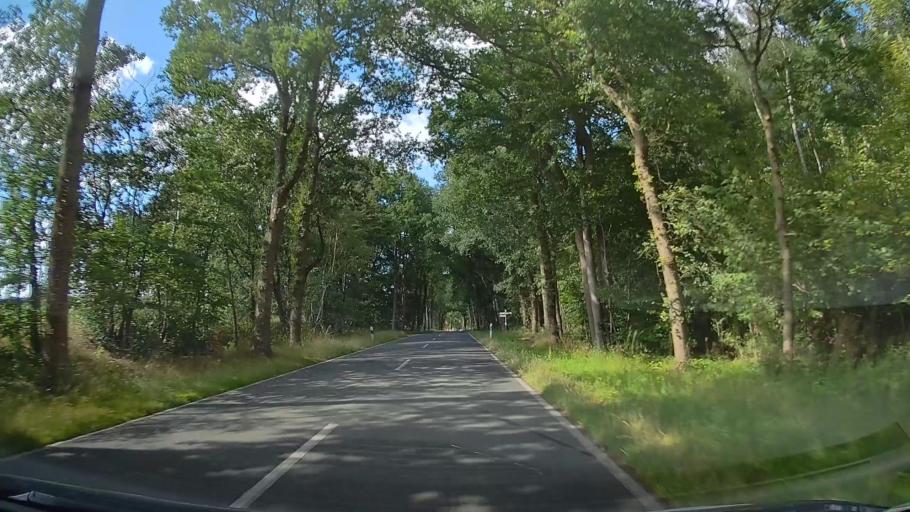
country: DE
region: Lower Saxony
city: Bippen
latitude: 52.6010
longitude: 7.7423
